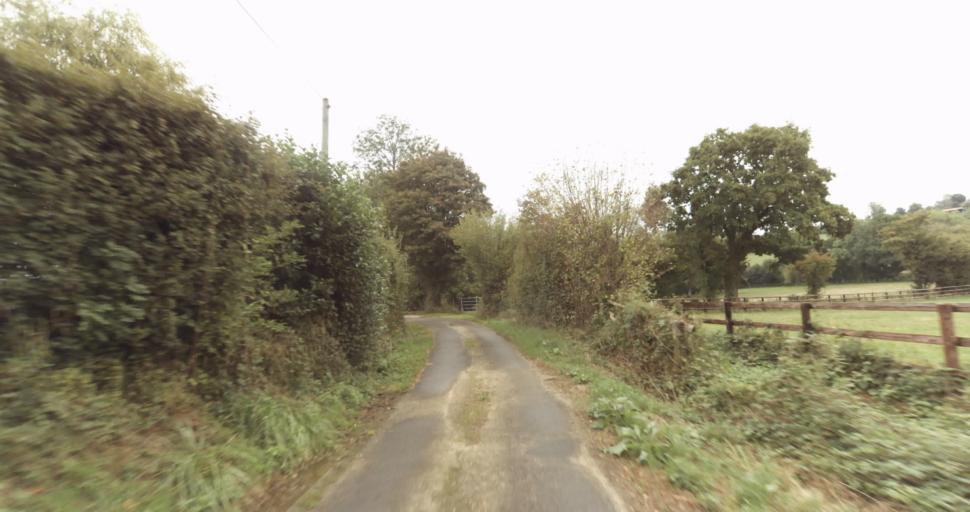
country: FR
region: Lower Normandy
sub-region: Departement de l'Orne
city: Gace
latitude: 48.7333
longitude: 0.3014
